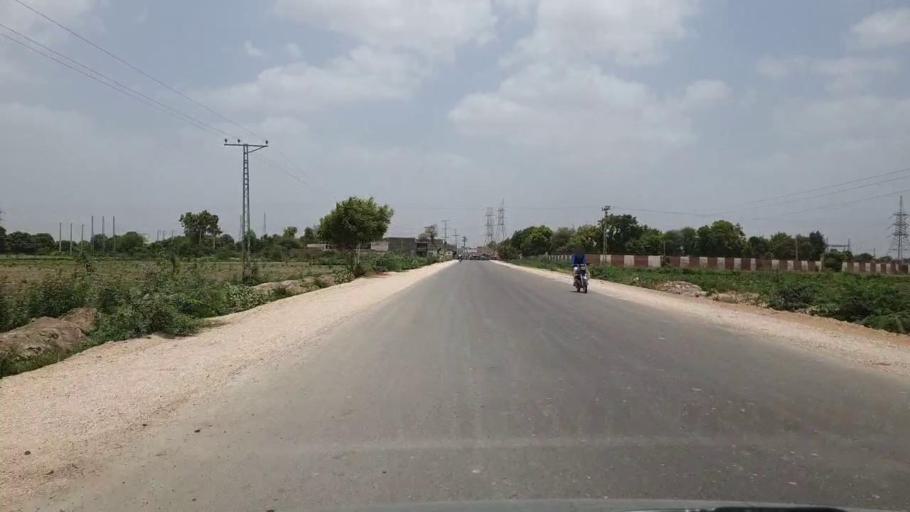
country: PK
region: Sindh
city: Naukot
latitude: 24.8502
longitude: 69.4103
